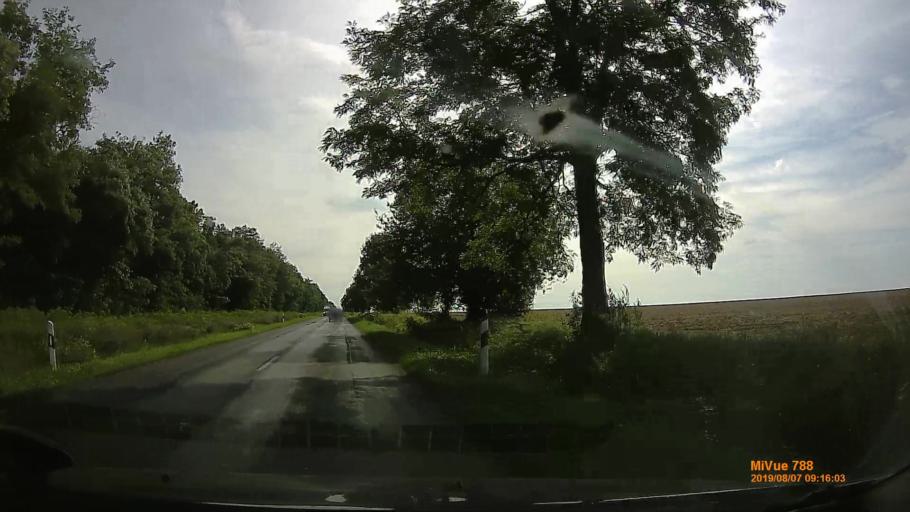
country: HU
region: Zala
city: Sarmellek
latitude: 46.7319
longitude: 17.1439
